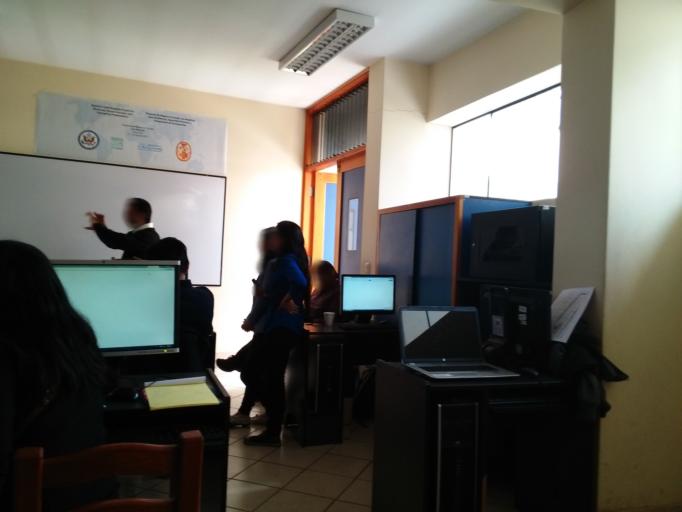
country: PE
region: Cusco
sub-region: Provincia de Cusco
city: Cusco
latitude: -13.5228
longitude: -71.9595
